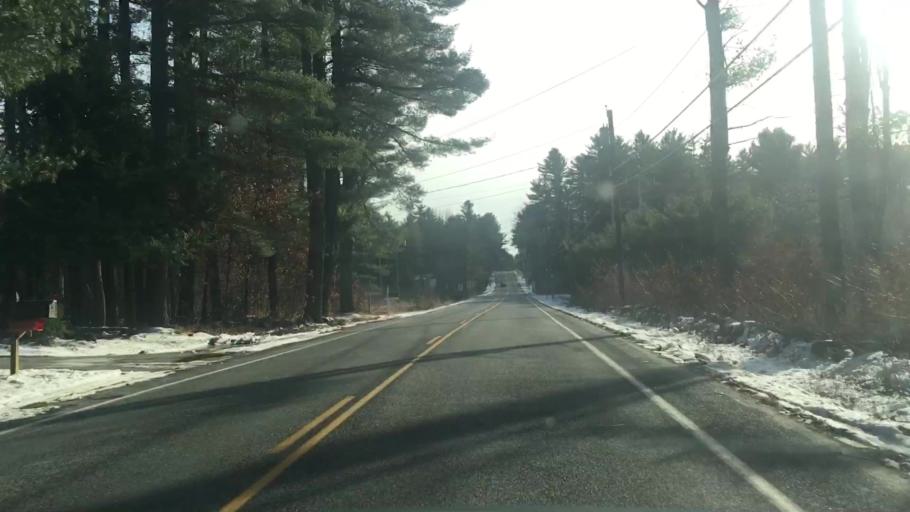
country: US
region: New Hampshire
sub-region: Merrimack County
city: Canterbury
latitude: 43.2920
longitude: -71.5621
